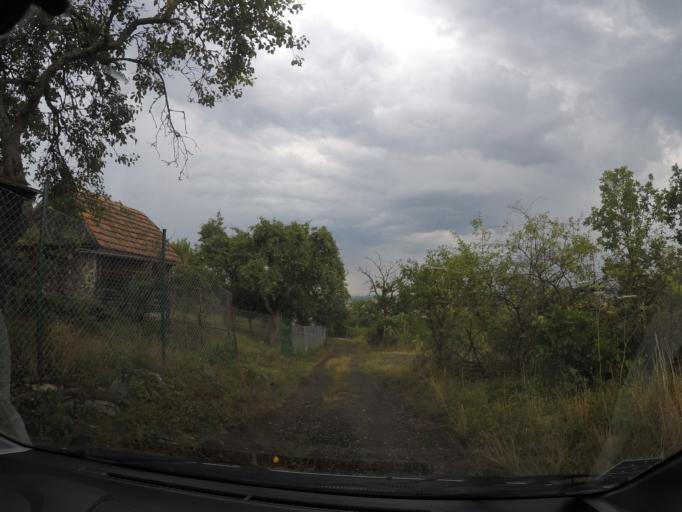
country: SK
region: Nitriansky
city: Tlmace
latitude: 48.3019
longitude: 18.5656
